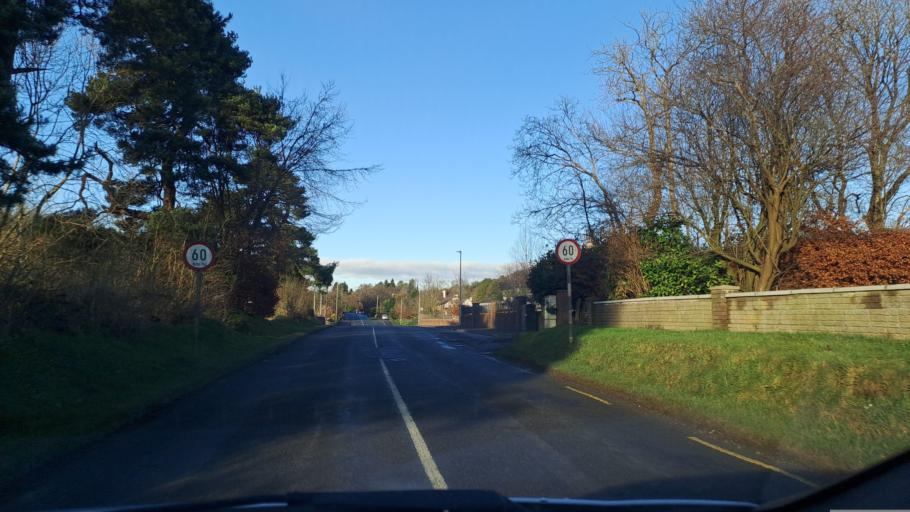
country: IE
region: Ulster
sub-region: An Cabhan
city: Bailieborough
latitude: 53.9076
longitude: -6.9672
